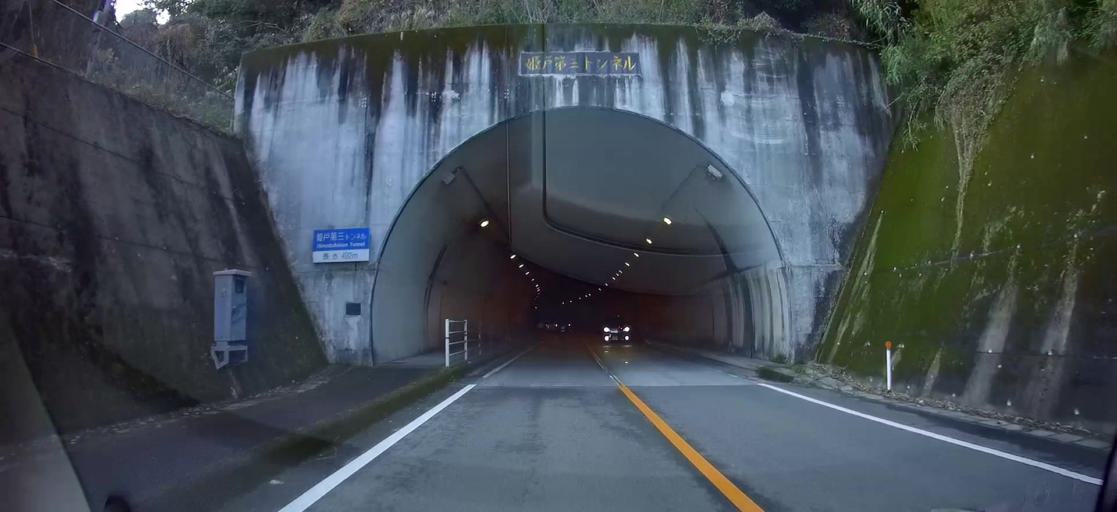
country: JP
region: Kumamoto
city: Yatsushiro
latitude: 32.4429
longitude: 130.4123
